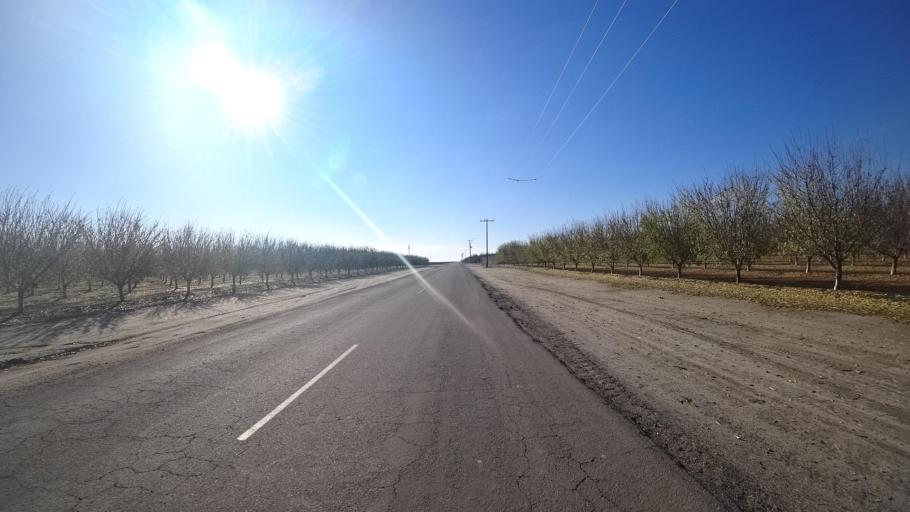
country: US
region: California
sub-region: Kern County
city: Delano
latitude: 35.7376
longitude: -119.2763
